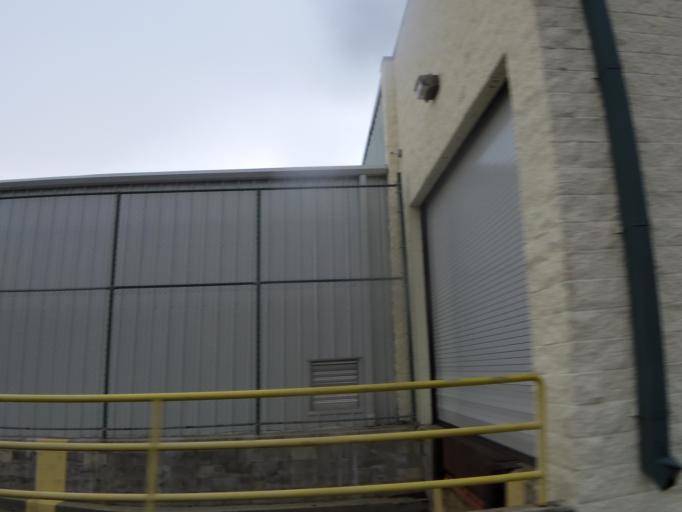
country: US
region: Florida
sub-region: Saint Johns County
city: Ponte Vedra Beach
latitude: 30.2532
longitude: -81.3937
